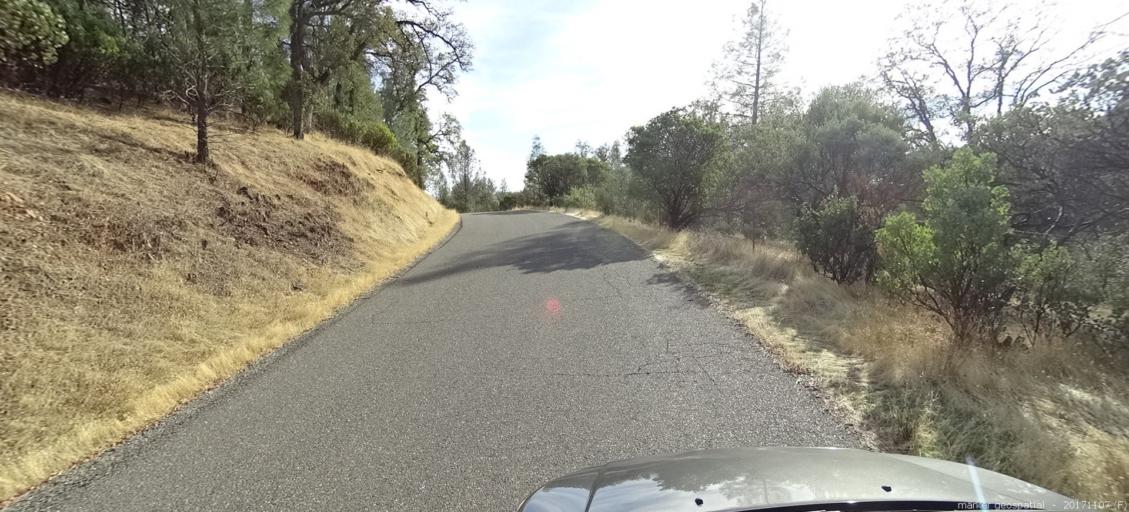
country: US
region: California
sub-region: Shasta County
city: Shasta
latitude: 40.5264
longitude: -122.5307
